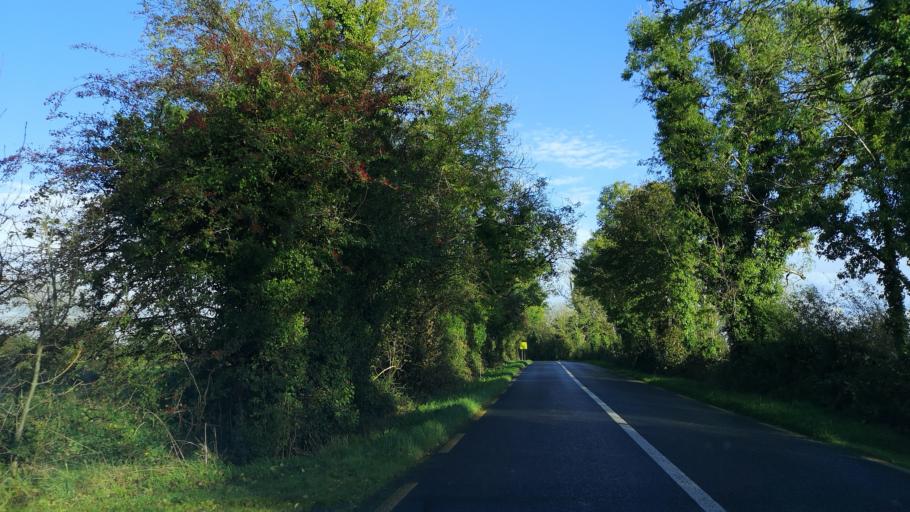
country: IE
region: Connaught
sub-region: Roscommon
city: Castlerea
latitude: 53.8212
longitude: -8.5524
